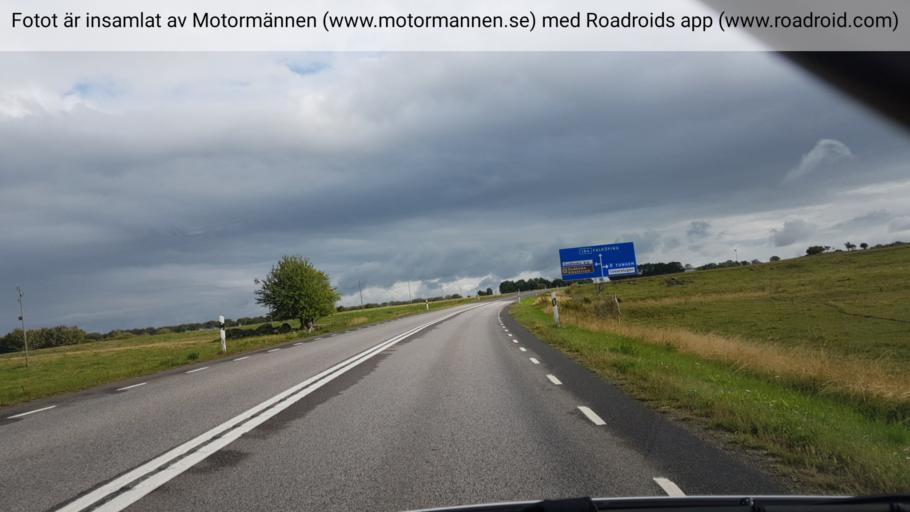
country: SE
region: Vaestra Goetaland
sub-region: Falkopings Kommun
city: Falkoeping
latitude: 58.2392
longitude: 13.5430
